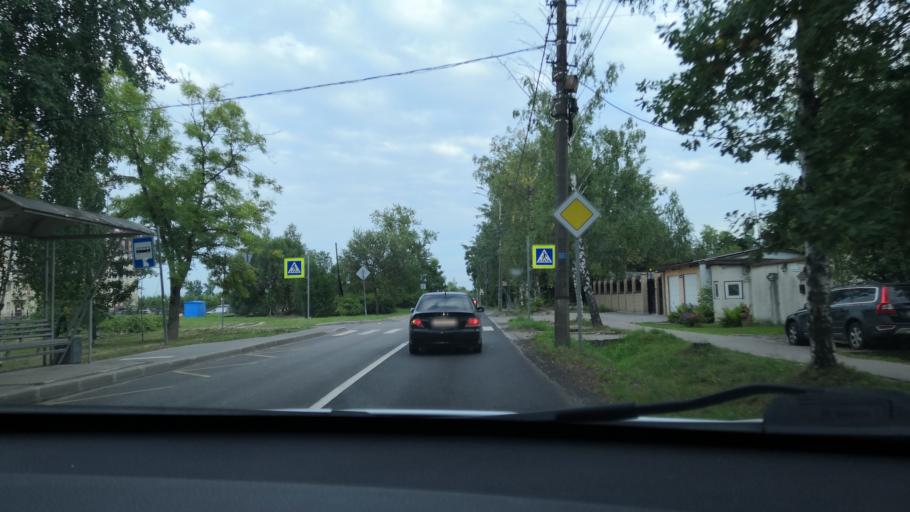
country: RU
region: St.-Petersburg
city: Pushkin
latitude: 59.6970
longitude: 30.4116
